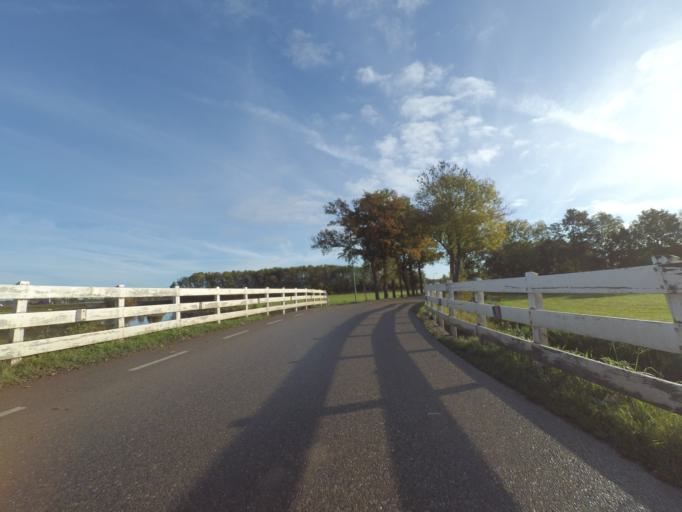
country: NL
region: Utrecht
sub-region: Gemeente Utrechtse Heuvelrug
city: Driebergen-Rijsenburg
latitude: 52.0106
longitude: 5.2678
